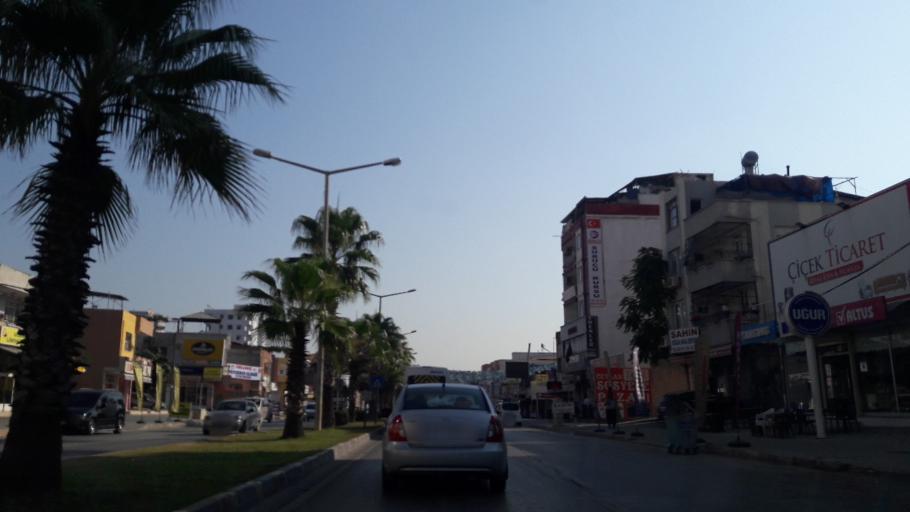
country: TR
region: Adana
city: Yuregir
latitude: 37.0332
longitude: 35.4126
